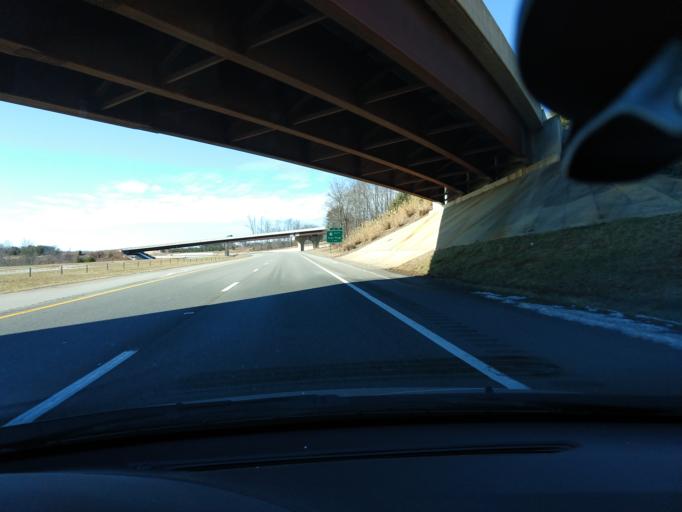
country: US
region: North Carolina
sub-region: Guilford County
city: Oak Ridge
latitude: 36.1226
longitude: -79.9313
